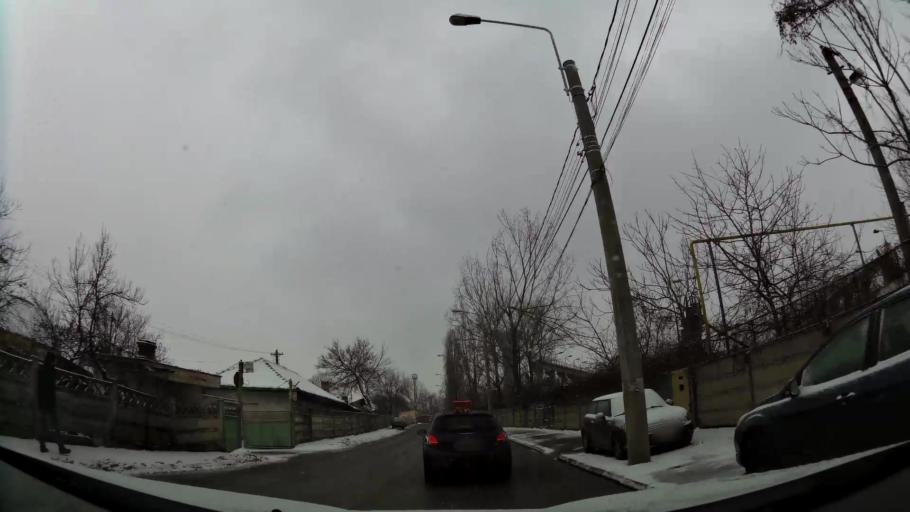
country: RO
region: Prahova
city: Ploiesti
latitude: 44.9244
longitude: 26.0237
